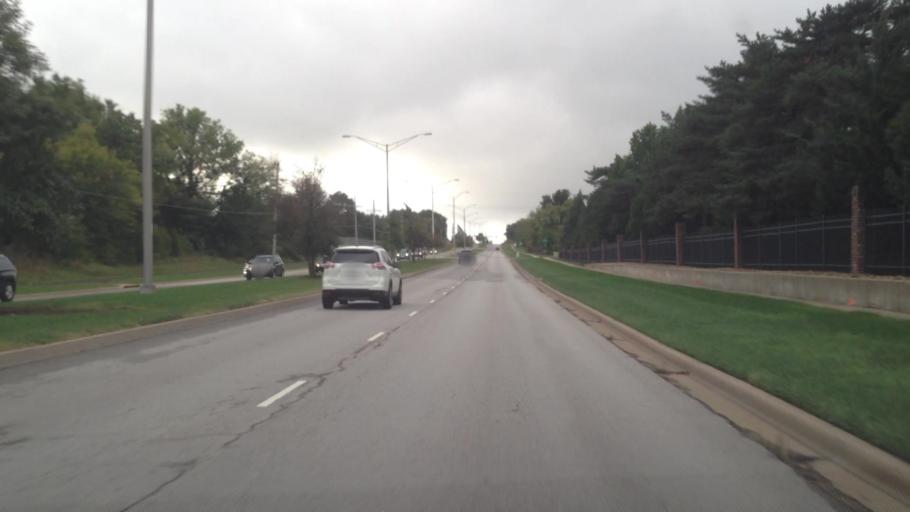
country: US
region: Kansas
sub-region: Johnson County
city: Lenexa
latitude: 38.9079
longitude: -94.7238
